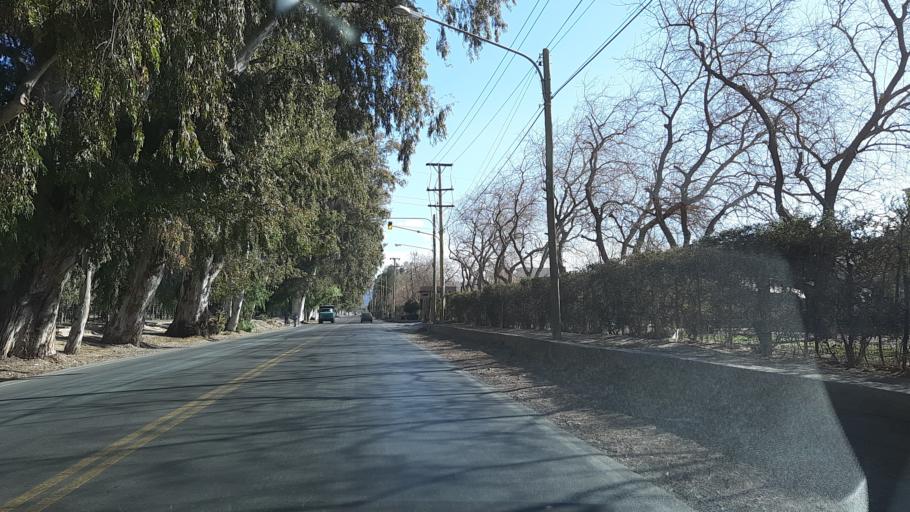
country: AR
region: San Juan
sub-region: Departamento de Rivadavia
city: Rivadavia
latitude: -31.5389
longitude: -68.6028
